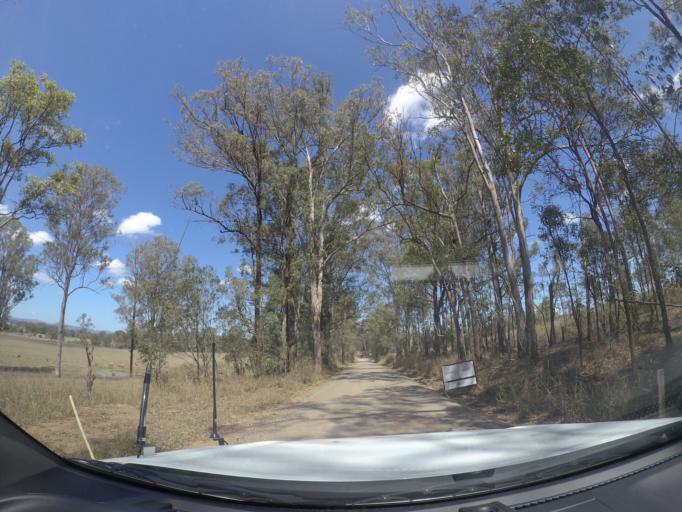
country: AU
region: Queensland
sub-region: Logan
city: North Maclean
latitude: -27.8375
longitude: 152.9248
